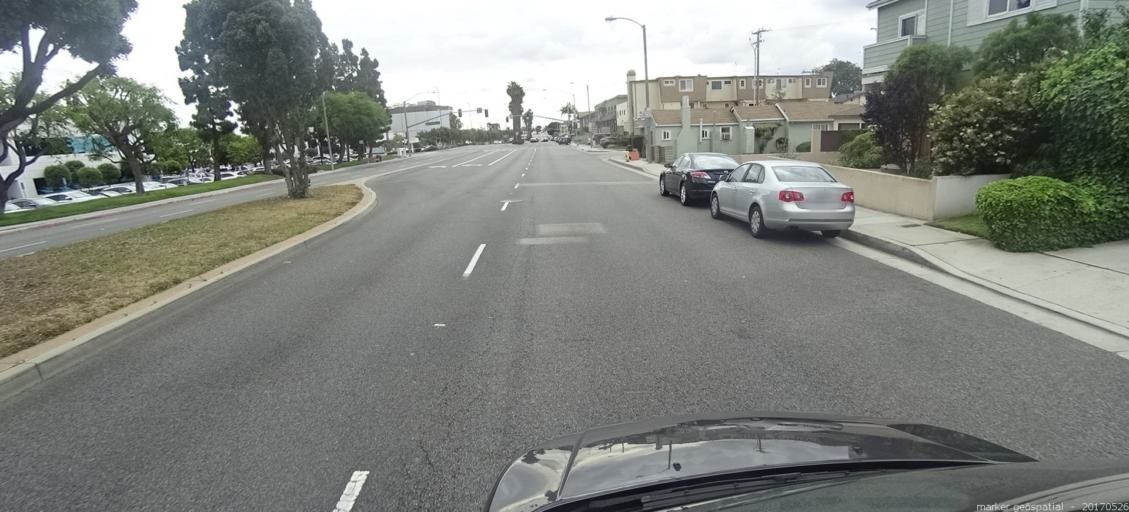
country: US
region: California
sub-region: Los Angeles County
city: Lawndale
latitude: 33.8873
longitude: -118.3756
